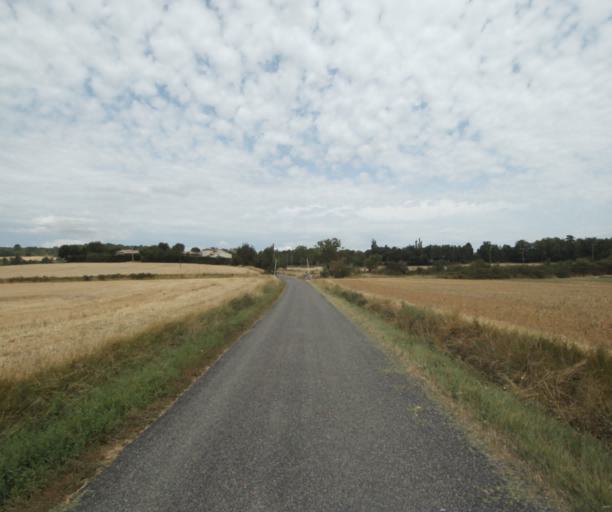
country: FR
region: Midi-Pyrenees
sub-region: Departement de la Haute-Garonne
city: Saint-Felix-Lauragais
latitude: 43.4230
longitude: 1.9000
